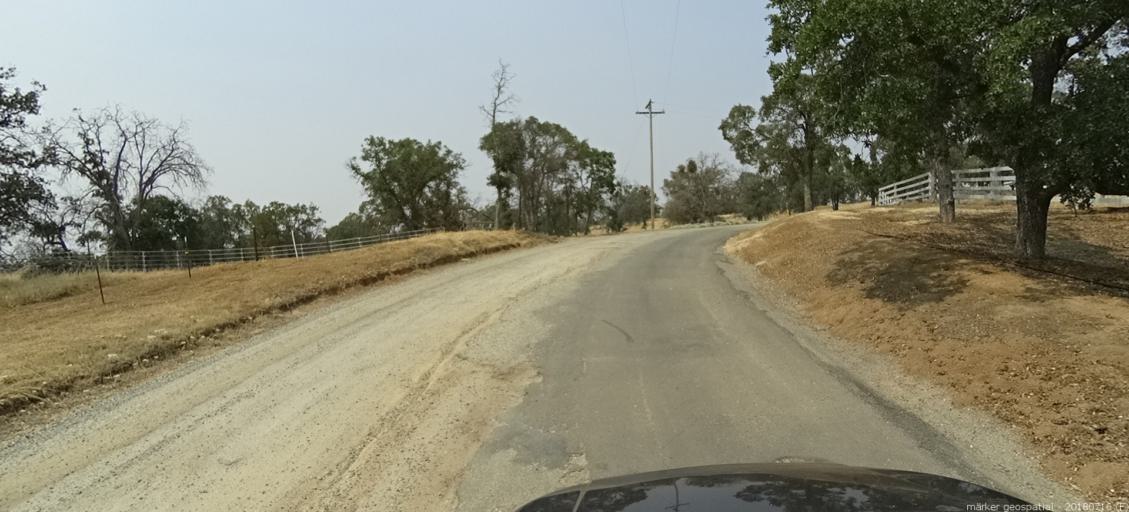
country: US
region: California
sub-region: Madera County
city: Yosemite Lakes
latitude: 37.2332
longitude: -119.7921
